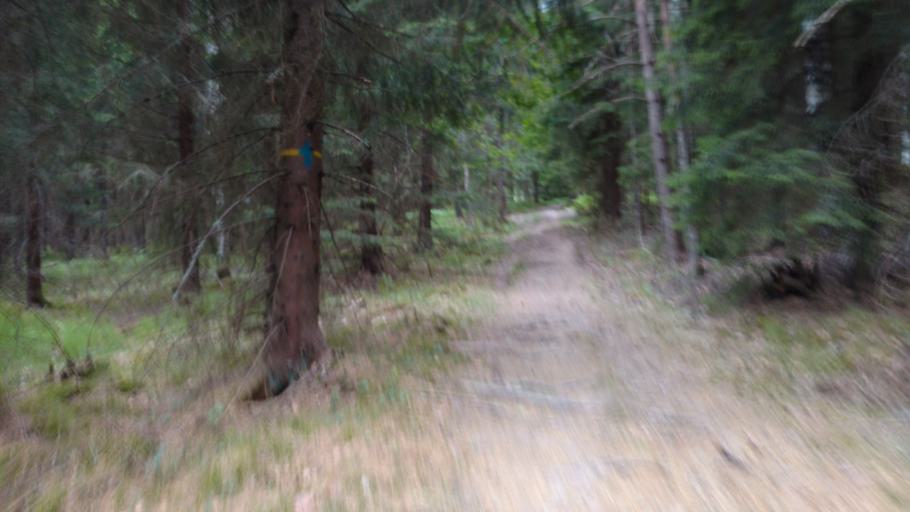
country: FI
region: Uusimaa
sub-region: Raaseporin
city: Pohja
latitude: 60.1188
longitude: 23.5627
